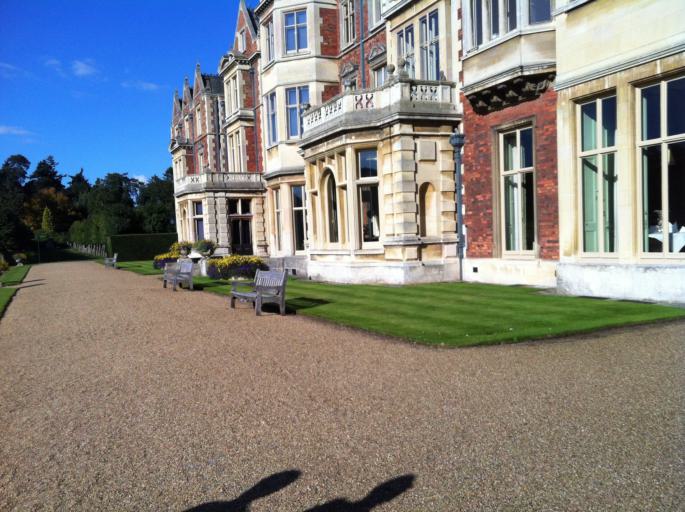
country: GB
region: England
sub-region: Norfolk
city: Dersingham
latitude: 52.8297
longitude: 0.5134
